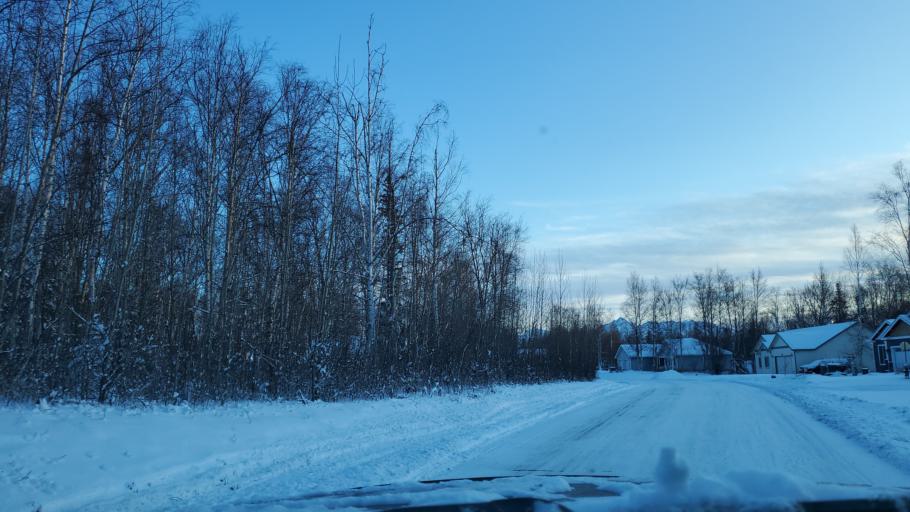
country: US
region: Alaska
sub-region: Matanuska-Susitna Borough
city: Lakes
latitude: 61.6367
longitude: -149.3131
